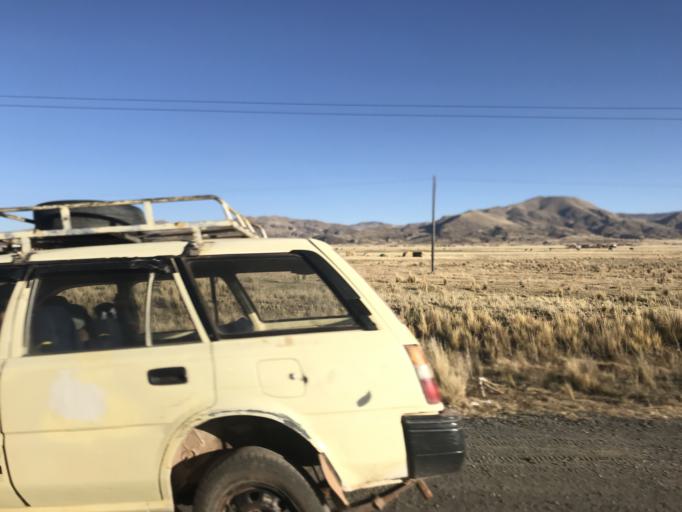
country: BO
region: La Paz
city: Tiahuanaco
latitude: -16.5686
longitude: -68.6581
